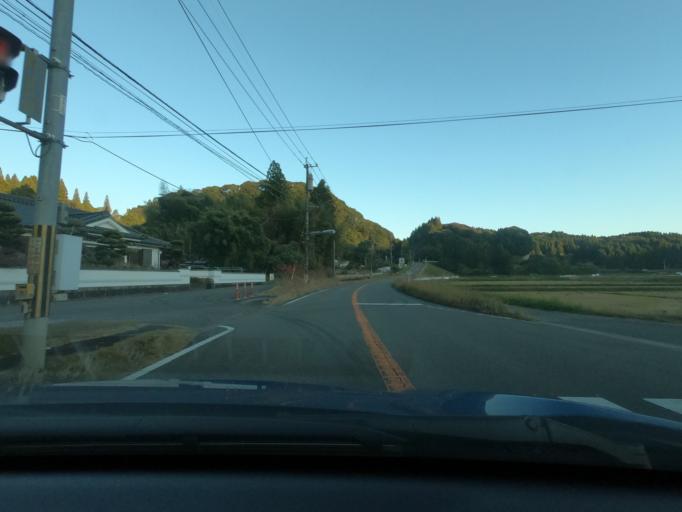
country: JP
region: Kagoshima
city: Satsumasendai
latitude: 31.8074
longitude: 130.3892
